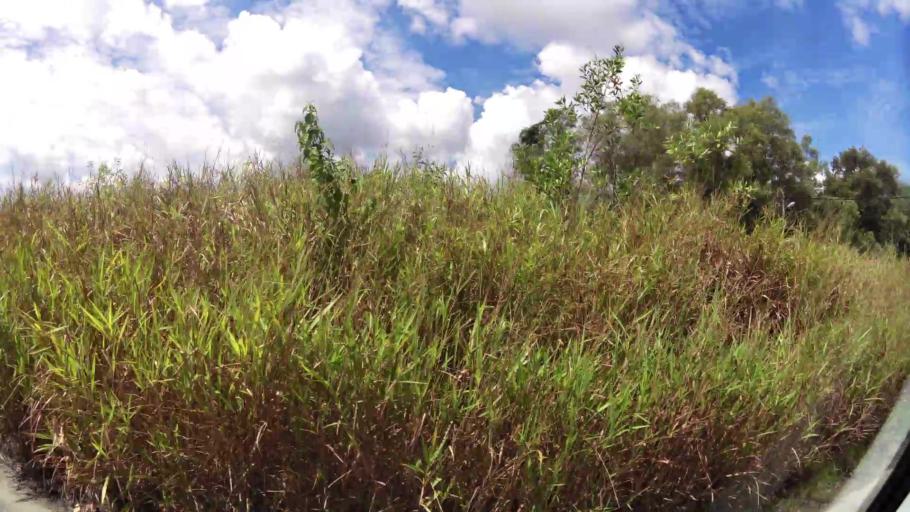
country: BN
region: Brunei and Muara
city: Bandar Seri Begawan
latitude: 4.9410
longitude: 114.9042
